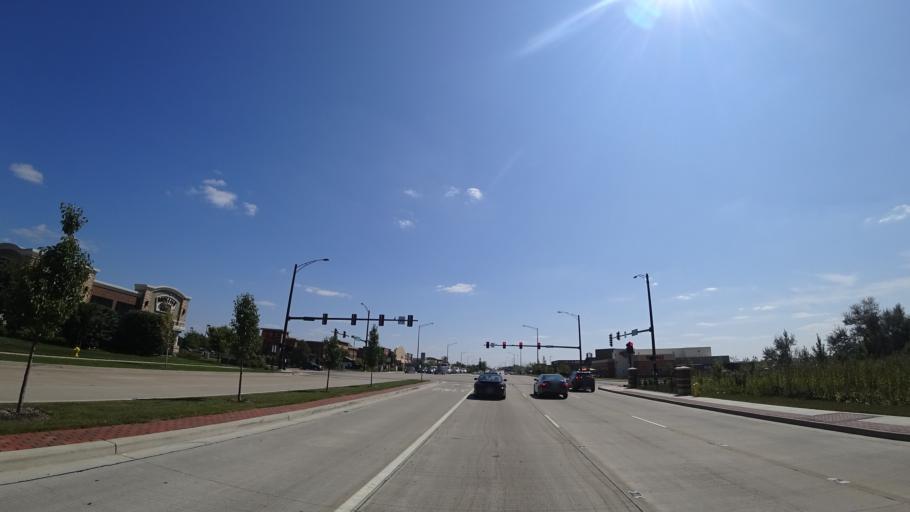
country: US
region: Illinois
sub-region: Cook County
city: Orland Park
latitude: 41.6114
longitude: -87.8538
